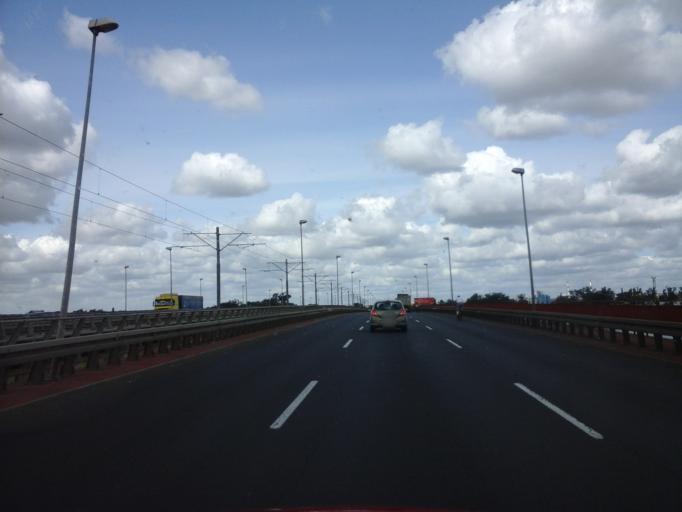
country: PL
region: West Pomeranian Voivodeship
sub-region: Szczecin
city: Szczecin
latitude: 53.3932
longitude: 14.6146
